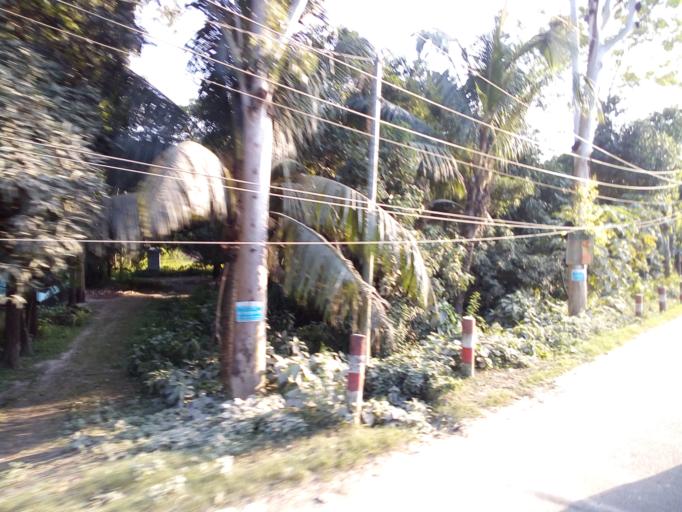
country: BD
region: Dhaka
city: Nagarpur
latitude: 23.8739
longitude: 90.0139
